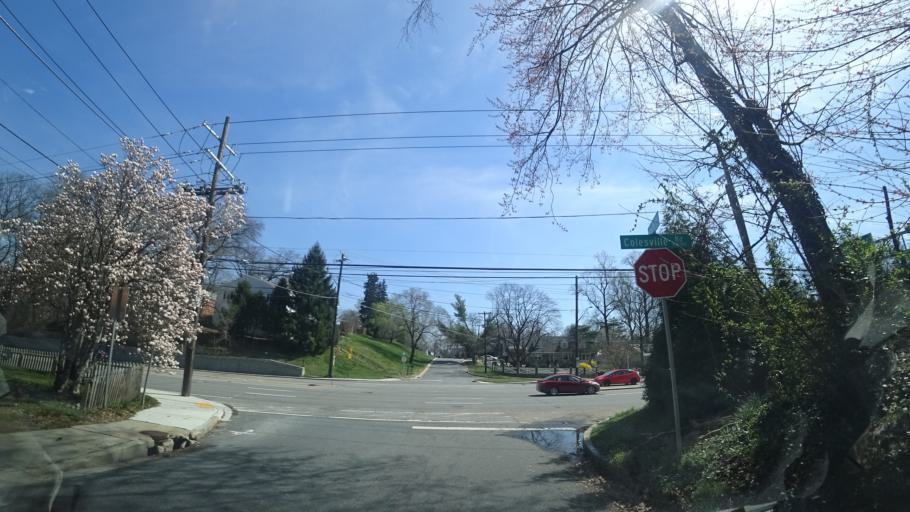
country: US
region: Maryland
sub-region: Montgomery County
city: Four Corners
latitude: 39.0240
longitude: -77.0115
